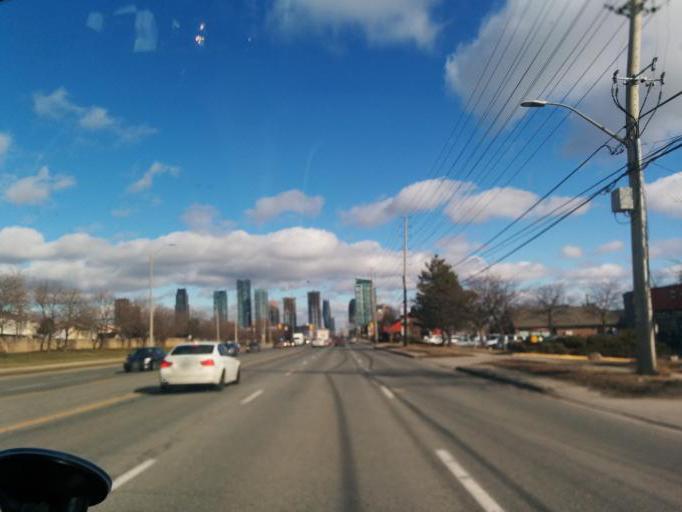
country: CA
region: Ontario
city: Mississauga
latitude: 43.5747
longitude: -79.6569
